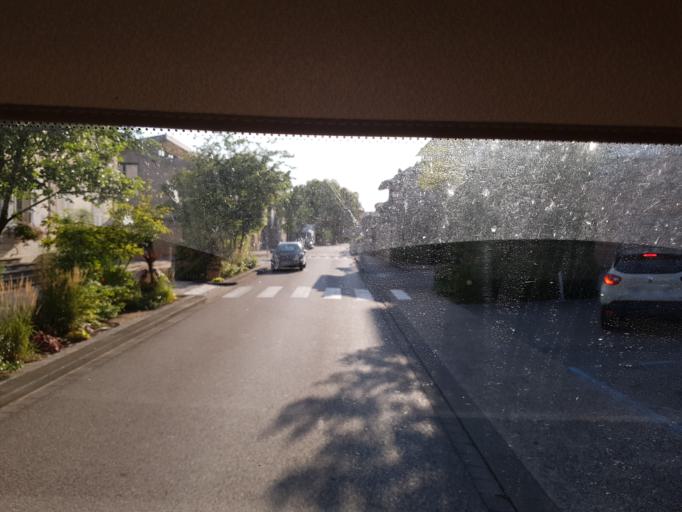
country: FR
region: Rhone-Alpes
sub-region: Departement de l'Ain
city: Neuville-sur-Ain
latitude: 46.0494
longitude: 5.3410
